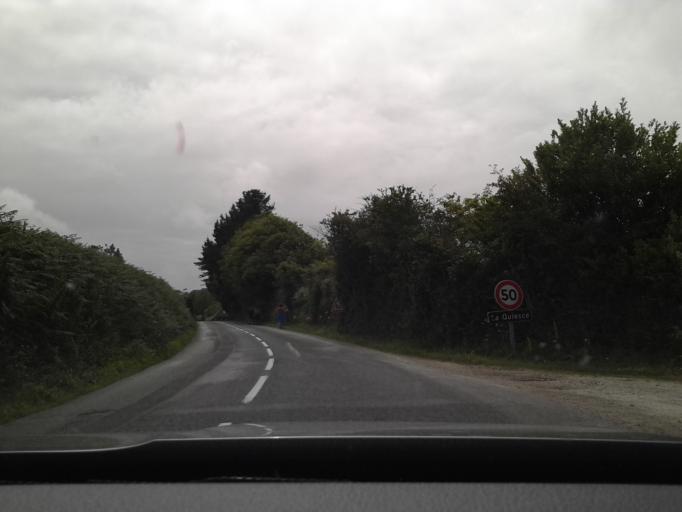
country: FR
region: Lower Normandy
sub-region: Departement de la Manche
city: Urville-Nacqueville
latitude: 49.6772
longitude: -1.7785
